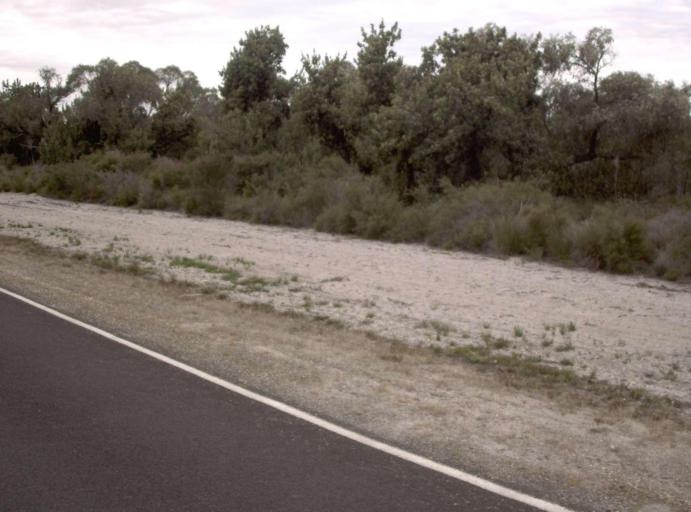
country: AU
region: Victoria
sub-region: Wellington
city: Sale
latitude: -38.1731
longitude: 147.3828
